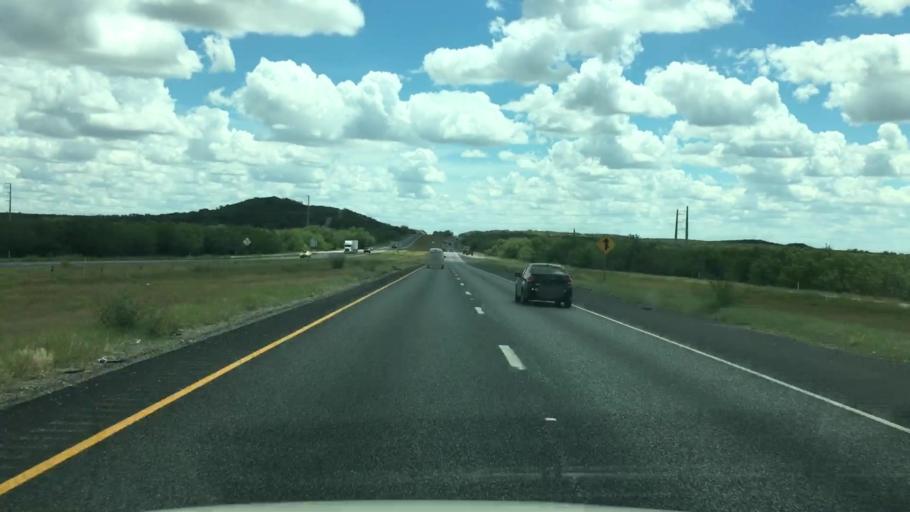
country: US
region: Texas
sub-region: Live Oak County
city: Three Rivers
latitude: 28.7304
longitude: -98.2882
